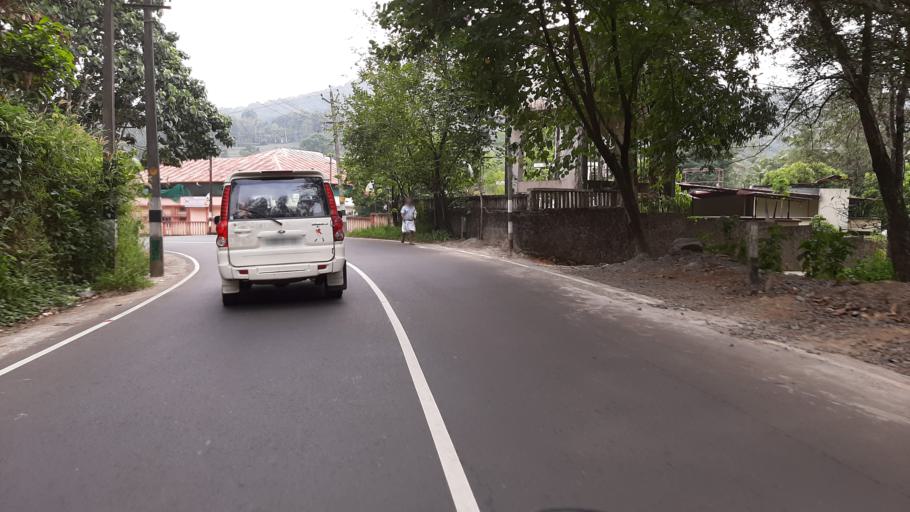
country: IN
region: Kerala
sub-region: Pattanamtitta
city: Pathanamthitta
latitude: 9.4498
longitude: 76.8718
